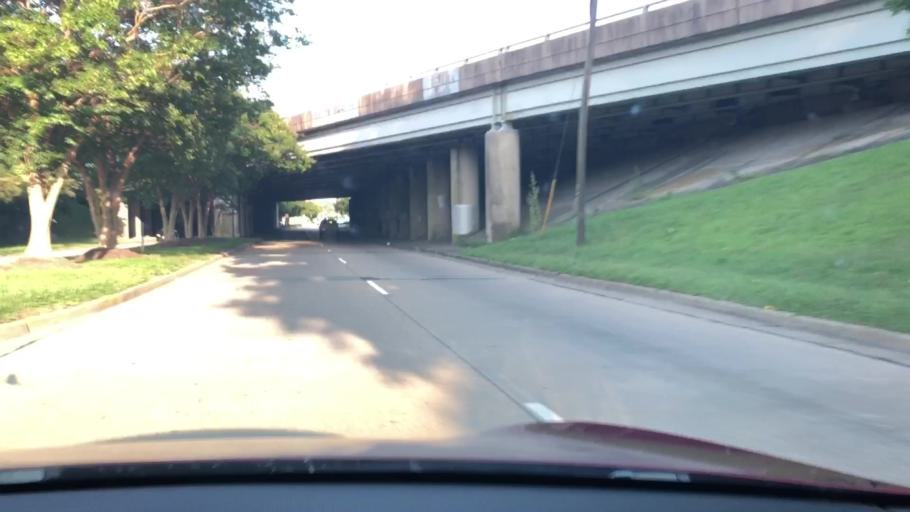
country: US
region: Virginia
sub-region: City of Virginia Beach
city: Virginia Beach
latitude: 36.8435
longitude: -76.0321
